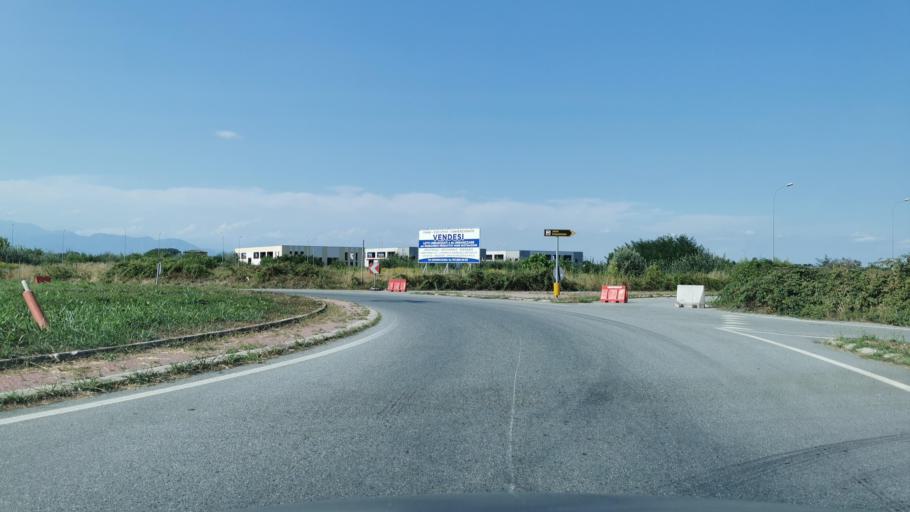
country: IT
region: Piedmont
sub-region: Provincia di Cuneo
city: Carde
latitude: 44.7345
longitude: 7.4219
